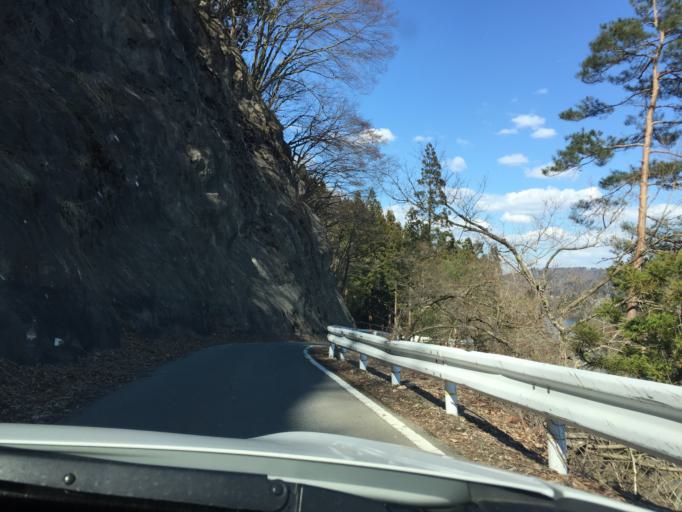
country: JP
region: Yamagata
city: Nagai
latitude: 38.2632
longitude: 140.1066
